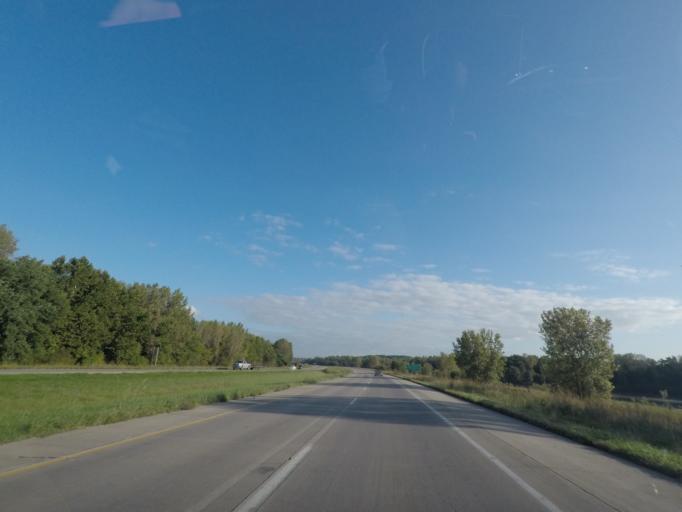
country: US
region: Iowa
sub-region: Polk County
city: Pleasant Hill
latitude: 41.5547
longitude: -93.5105
